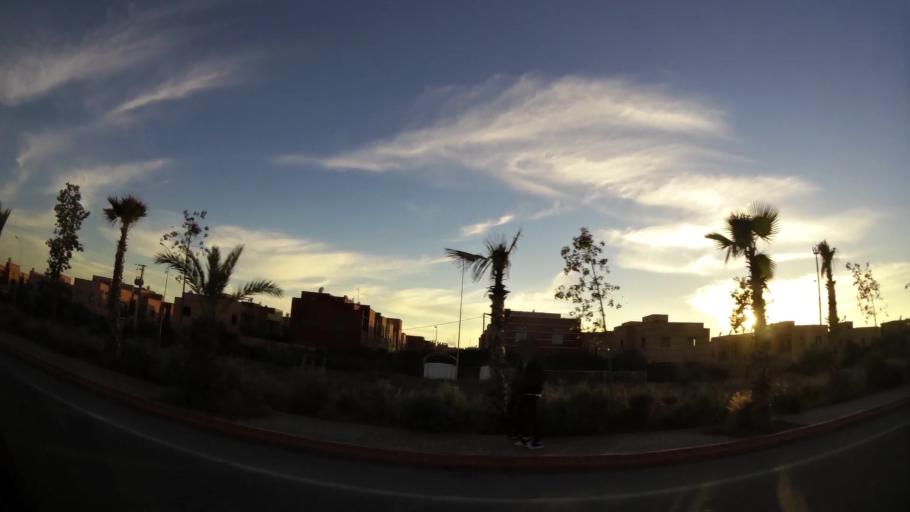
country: MA
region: Marrakech-Tensift-Al Haouz
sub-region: Marrakech
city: Marrakesh
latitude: 31.7496
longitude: -8.1080
